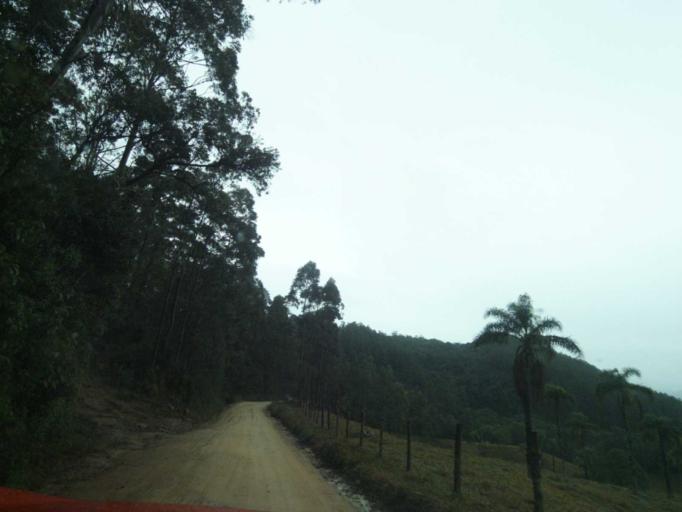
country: BR
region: Santa Catarina
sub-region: Anitapolis
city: Anitapolis
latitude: -27.9179
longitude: -49.1747
